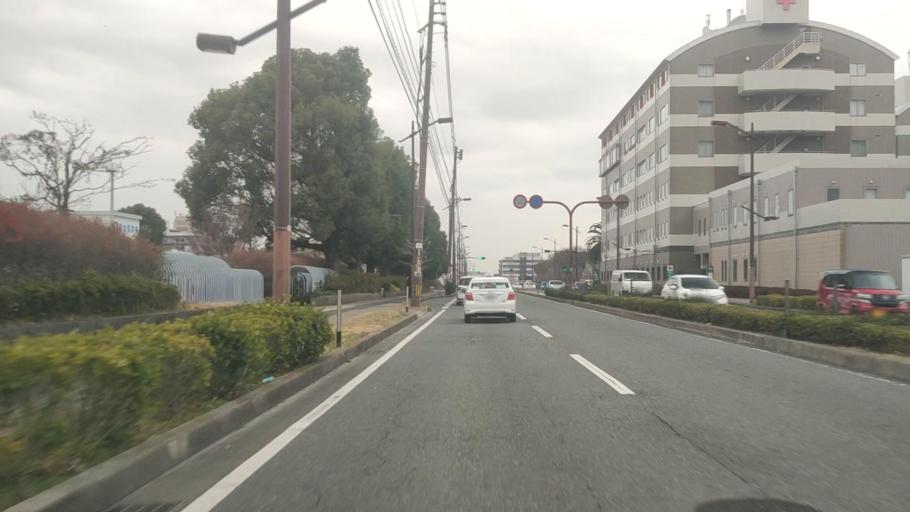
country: JP
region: Kumamoto
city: Kumamoto
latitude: 32.8077
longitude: 130.7658
